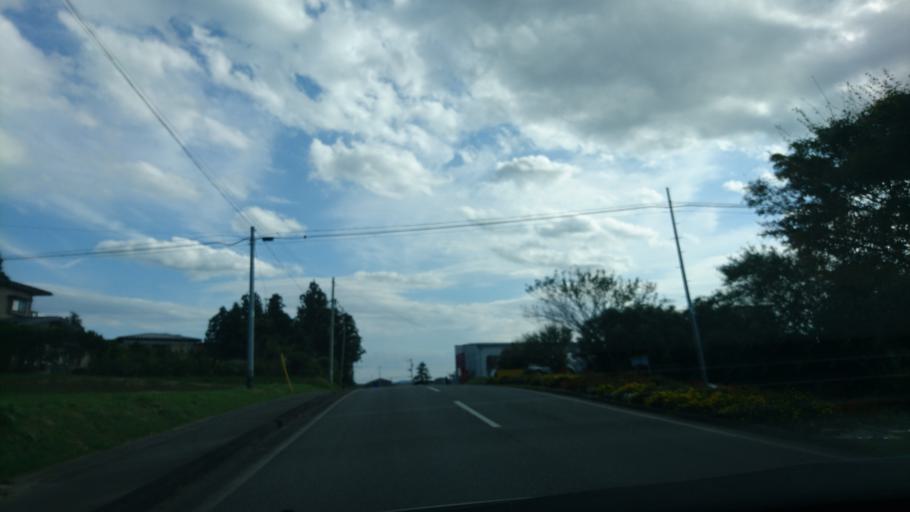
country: JP
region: Iwate
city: Ichinoseki
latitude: 38.8337
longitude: 141.1931
